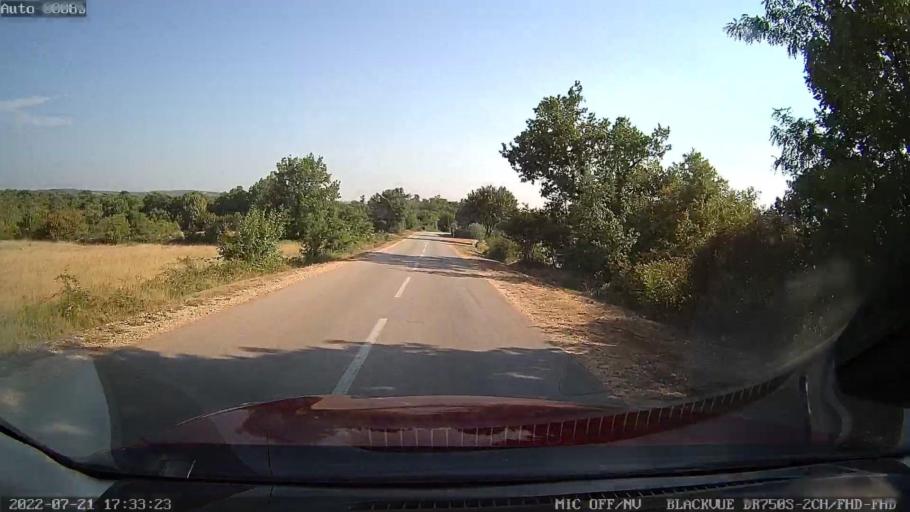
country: HR
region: Istarska
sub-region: Grad Rovinj
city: Rovinj
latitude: 45.1723
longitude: 13.7469
